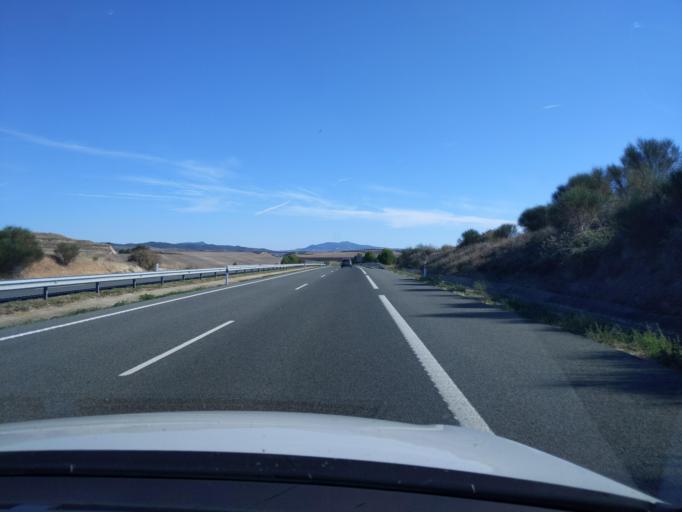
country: ES
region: Navarre
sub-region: Provincia de Navarra
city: Los Arcos
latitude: 42.5437
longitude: -2.2057
